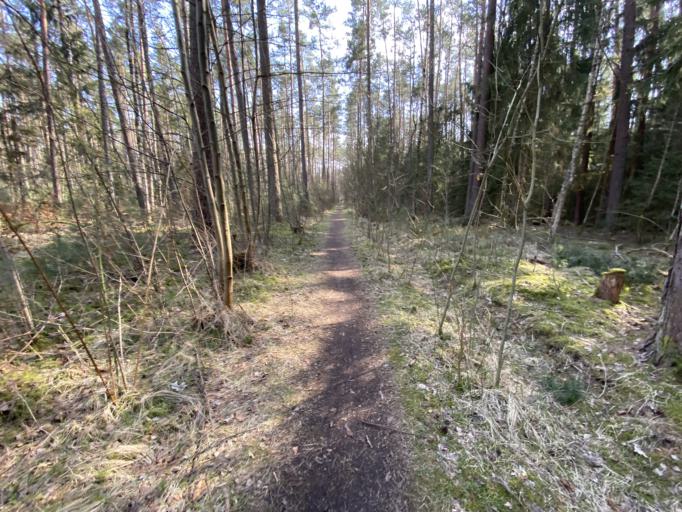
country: DE
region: Bavaria
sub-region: Regierungsbezirk Mittelfranken
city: Erlangen
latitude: 49.5649
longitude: 11.0248
